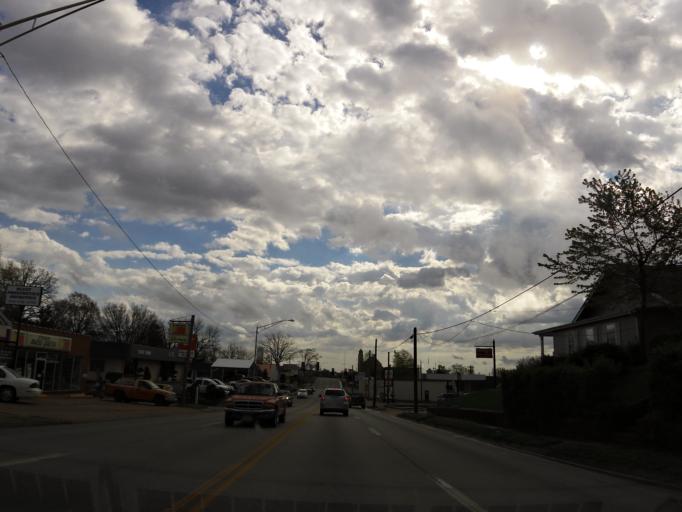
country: US
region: Missouri
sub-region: Butler County
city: Poplar Bluff
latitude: 36.7584
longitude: -90.4035
